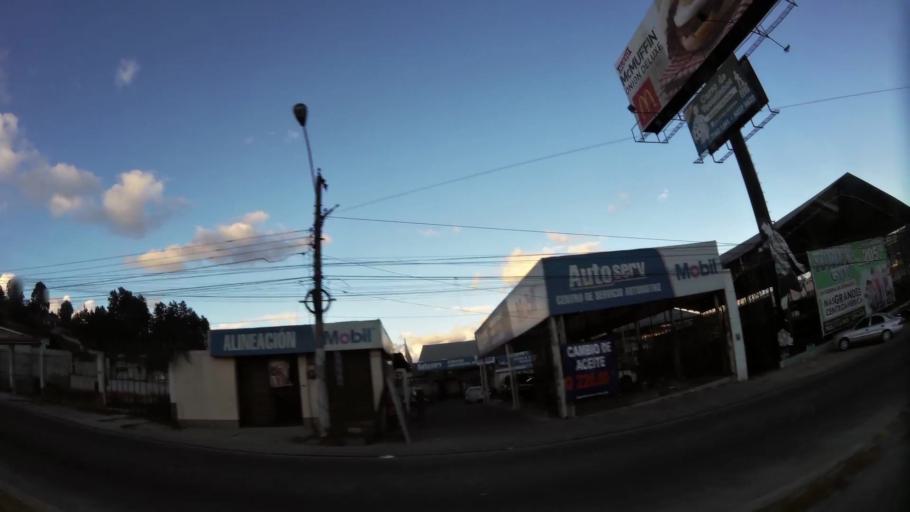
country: GT
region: Quetzaltenango
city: Quetzaltenango
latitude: 14.8421
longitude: -91.5116
